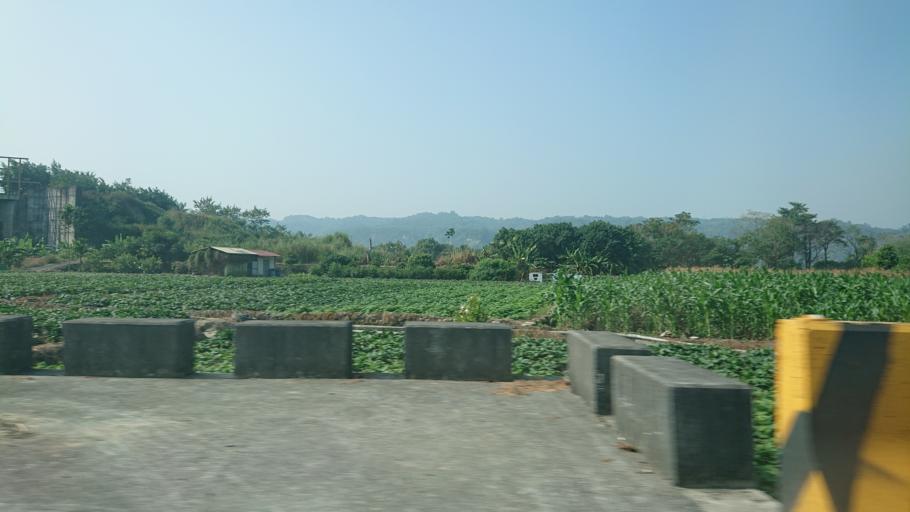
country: TW
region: Taiwan
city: Lugu
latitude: 23.7622
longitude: 120.6615
